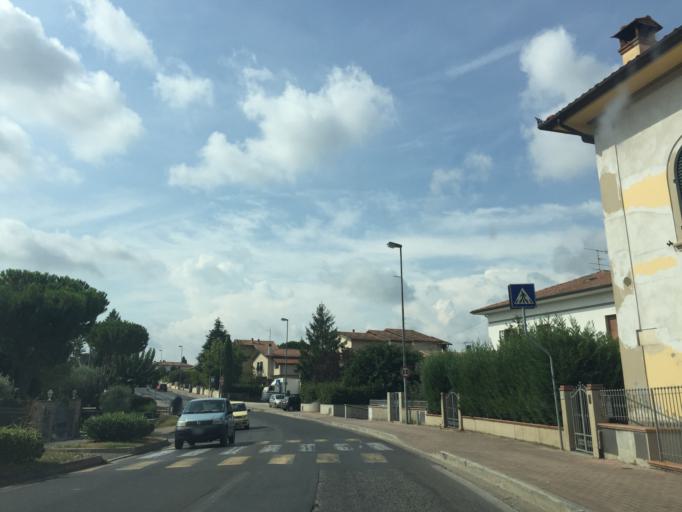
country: IT
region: Tuscany
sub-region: Province of Florence
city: Cerreto Guidi
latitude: 43.7549
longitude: 10.8822
